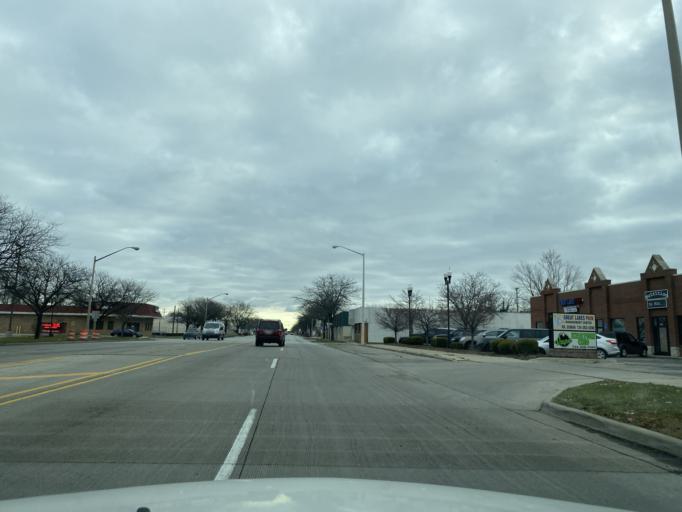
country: US
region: Michigan
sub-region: Wayne County
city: Southgate
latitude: 42.1994
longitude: -83.1798
